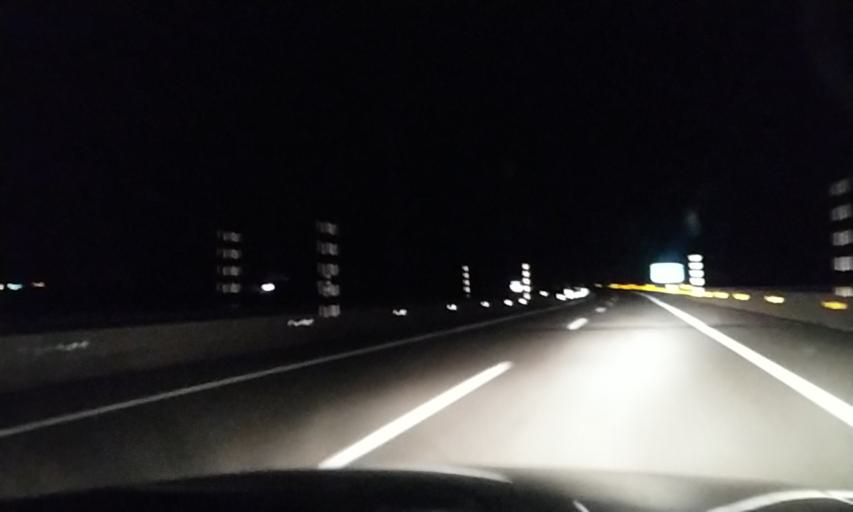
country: ES
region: Castille and Leon
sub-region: Provincia de Zamora
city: Puebla de Sanabria
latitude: 42.0607
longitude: -6.6162
